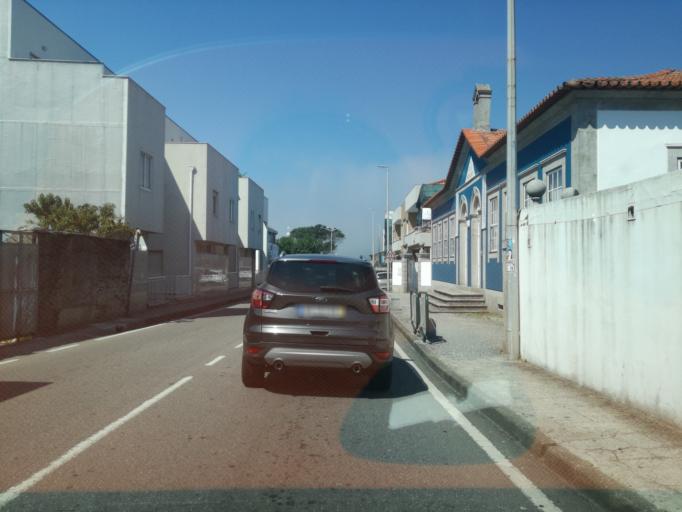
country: PT
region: Braga
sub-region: Esposende
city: Esposende
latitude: 41.5127
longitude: -8.7735
